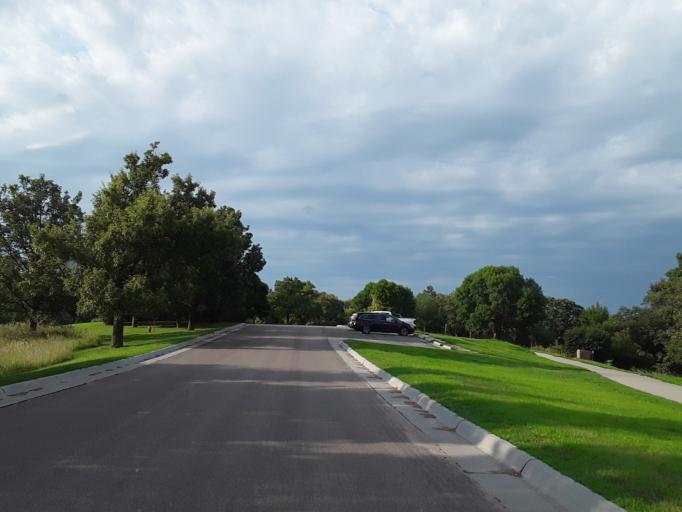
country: US
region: Nebraska
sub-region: Saunders County
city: Ashland
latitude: 41.0300
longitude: -96.3119
